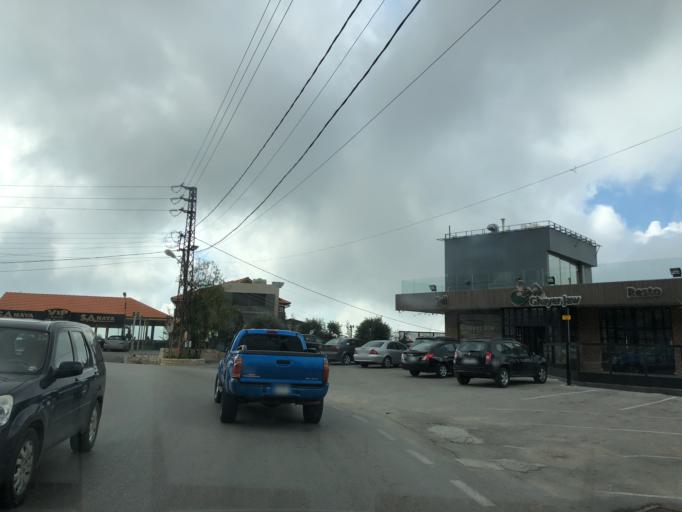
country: LB
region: Mont-Liban
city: Jbail
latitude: 34.1181
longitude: 35.7519
